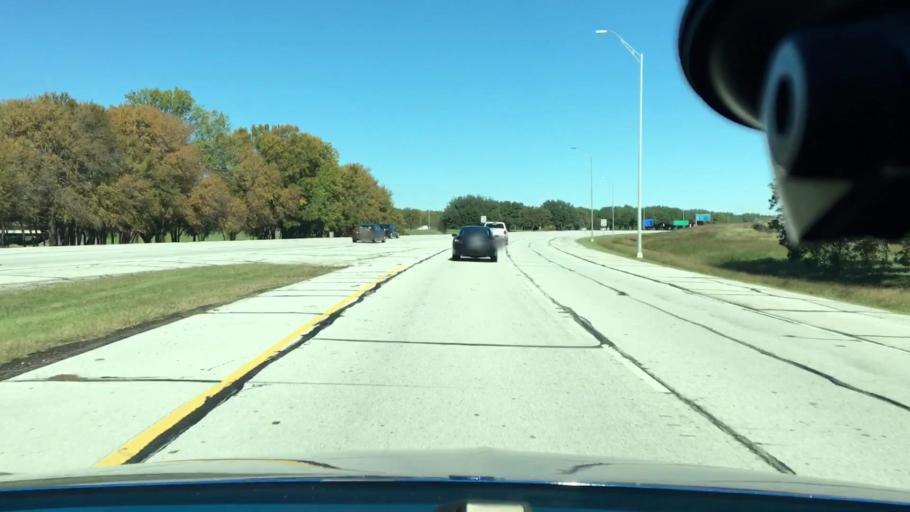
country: US
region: Texas
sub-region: Tarrant County
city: Euless
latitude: 32.8418
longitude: -97.0395
